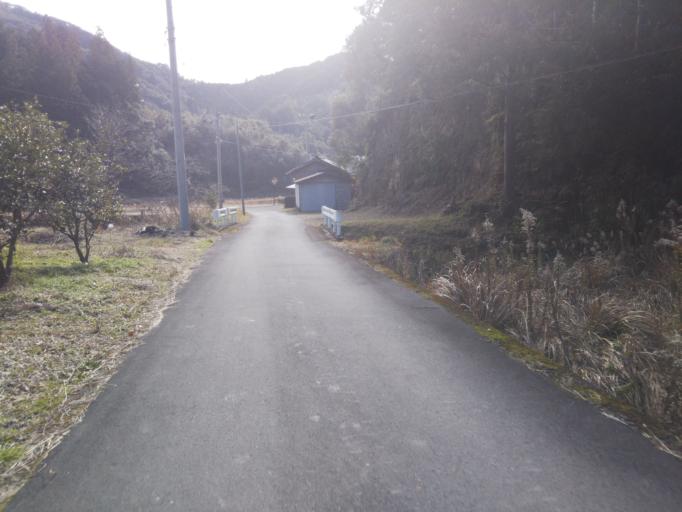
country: JP
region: Kochi
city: Nakamura
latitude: 33.0465
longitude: 132.9876
